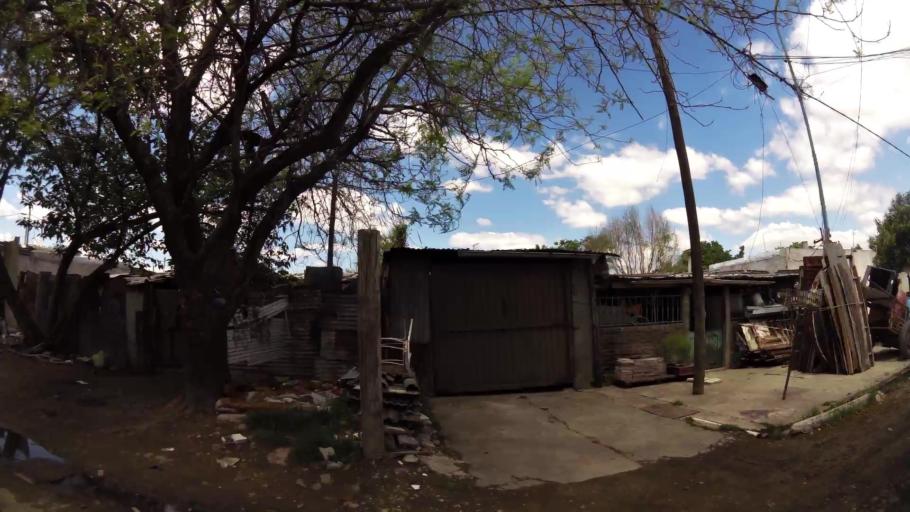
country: AR
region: Buenos Aires
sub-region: Partido de Lanus
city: Lanus
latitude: -34.7198
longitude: -58.4189
